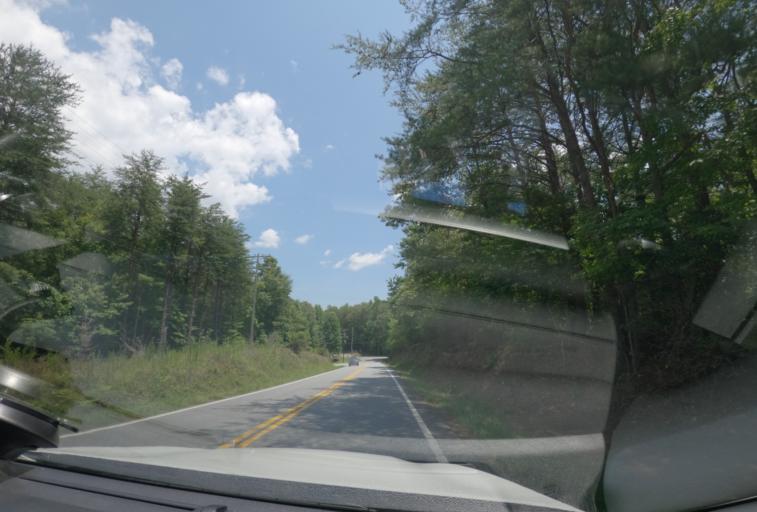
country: US
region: South Carolina
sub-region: Pickens County
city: Pickens
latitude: 34.9654
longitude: -82.8633
